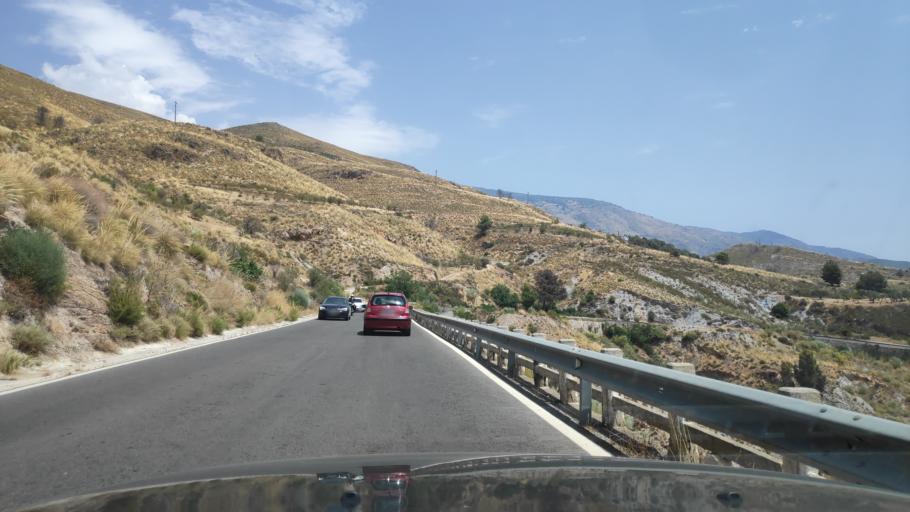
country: ES
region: Andalusia
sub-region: Provincia de Granada
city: Orjiva
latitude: 36.9060
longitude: -3.4522
